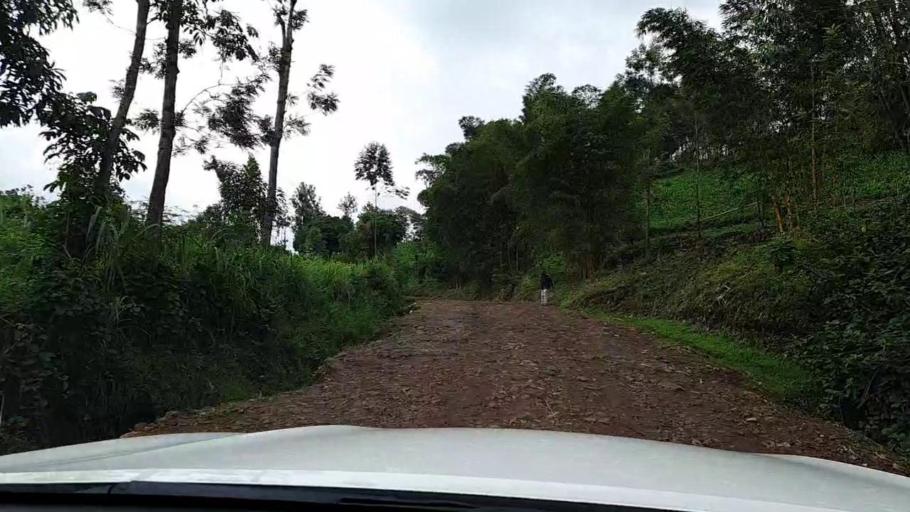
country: RW
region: Western Province
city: Cyangugu
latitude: -2.5628
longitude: 29.0360
